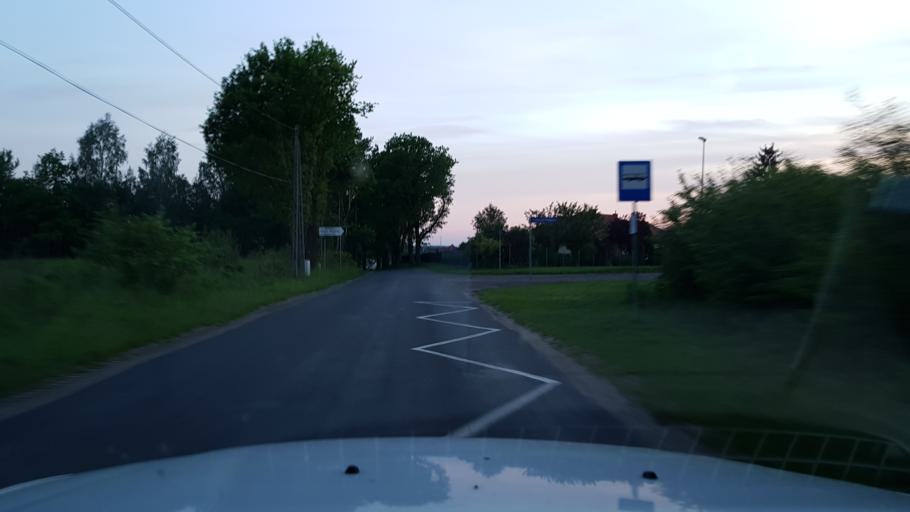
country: PL
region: West Pomeranian Voivodeship
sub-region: Powiat goleniowski
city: Goleniow
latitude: 53.5644
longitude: 14.8639
